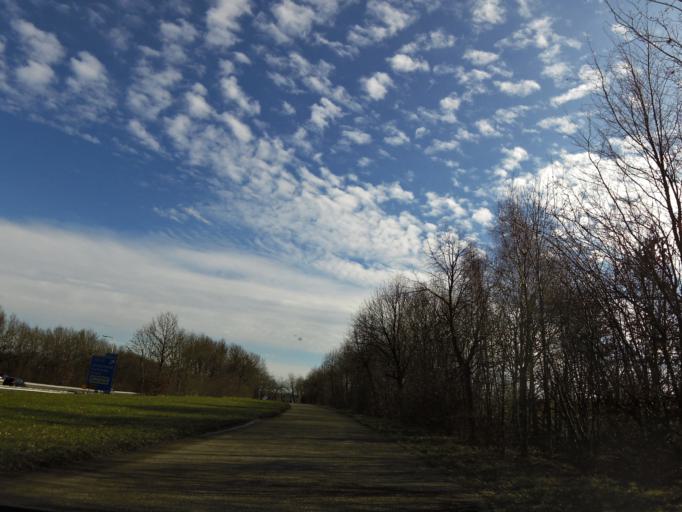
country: NL
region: Limburg
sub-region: Gemeente Simpelveld
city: Simpelveld
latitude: 50.8472
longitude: 5.9831
